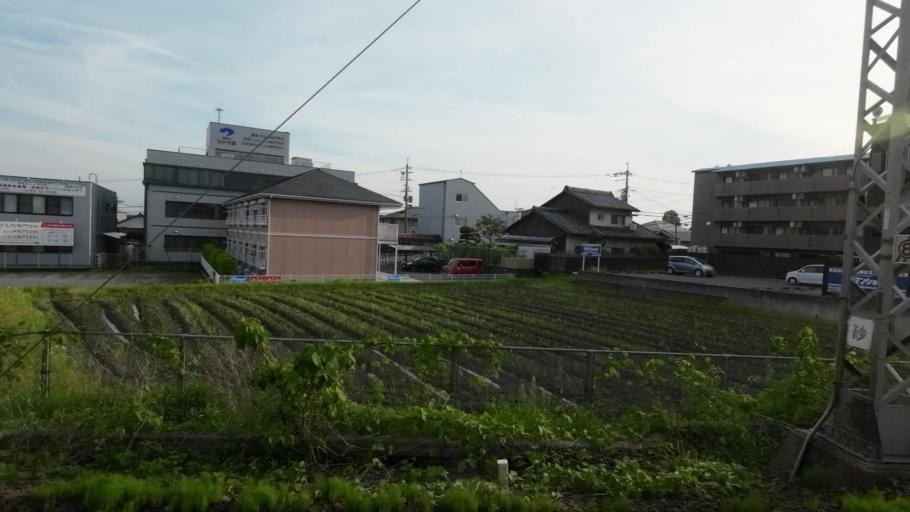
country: JP
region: Nara
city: Nara-shi
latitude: 34.6968
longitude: 135.7773
